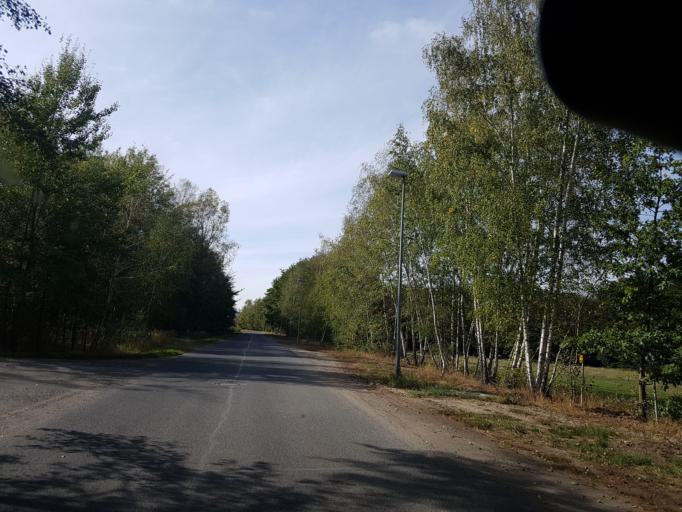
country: DE
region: Brandenburg
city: Doberlug-Kirchhain
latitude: 51.6321
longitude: 13.5854
